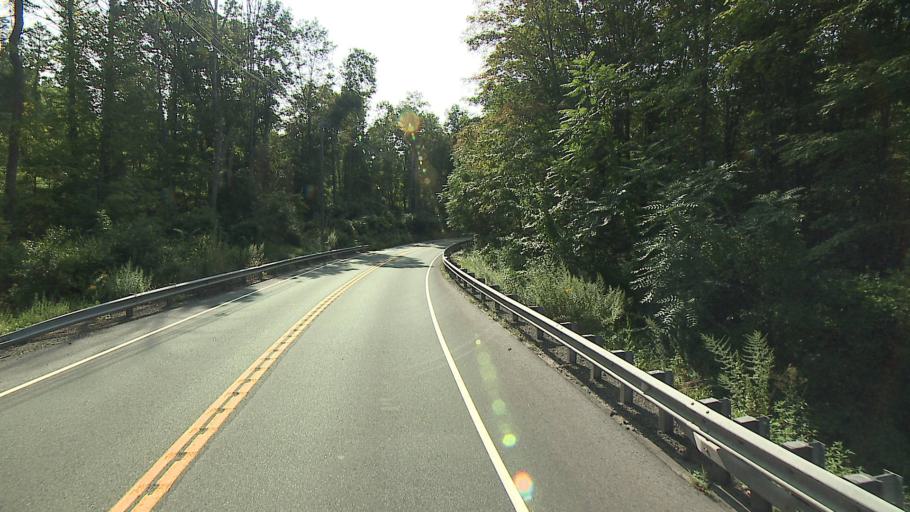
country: US
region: Connecticut
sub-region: Litchfield County
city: Kent
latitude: 41.6629
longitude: -73.4943
